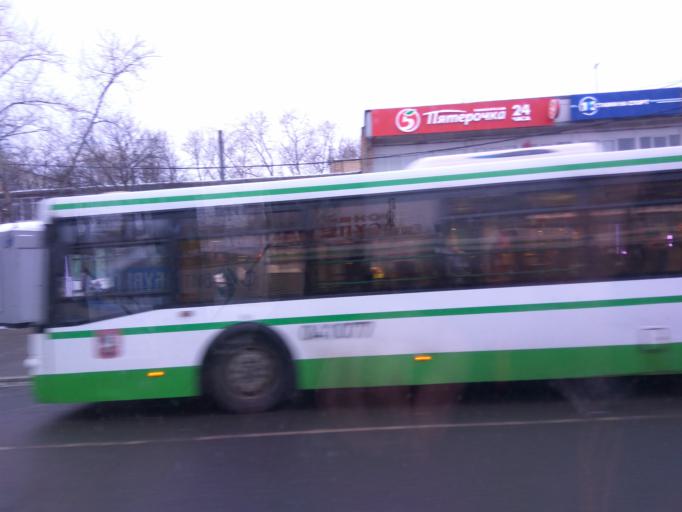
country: RU
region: Moscow
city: Metrogorodok
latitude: 55.8083
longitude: 37.7986
